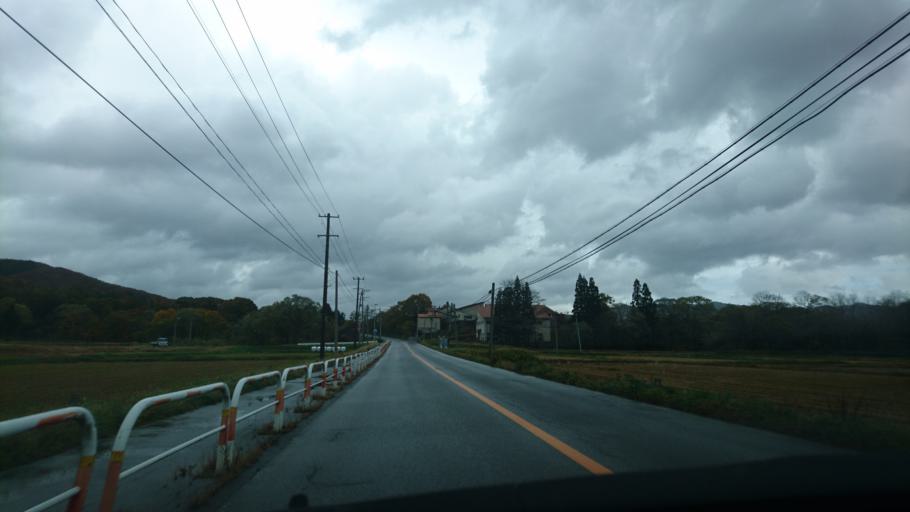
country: JP
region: Akita
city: Kakunodatemachi
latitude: 39.4492
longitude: 140.7633
